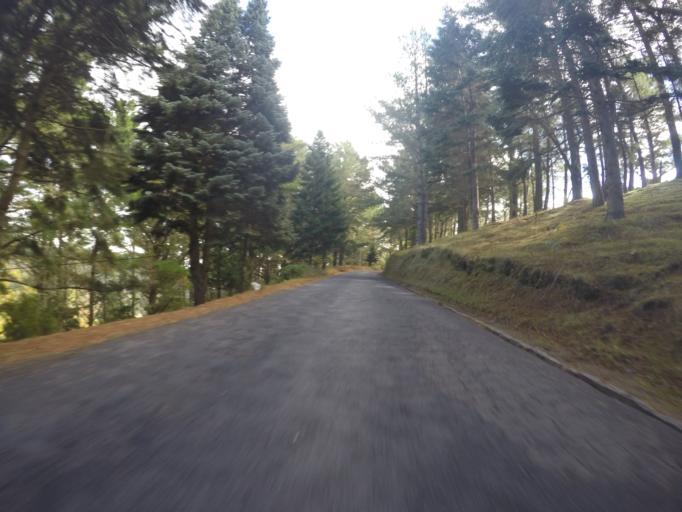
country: PT
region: Madeira
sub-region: Funchal
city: Nossa Senhora do Monte
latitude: 32.6963
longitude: -16.8795
